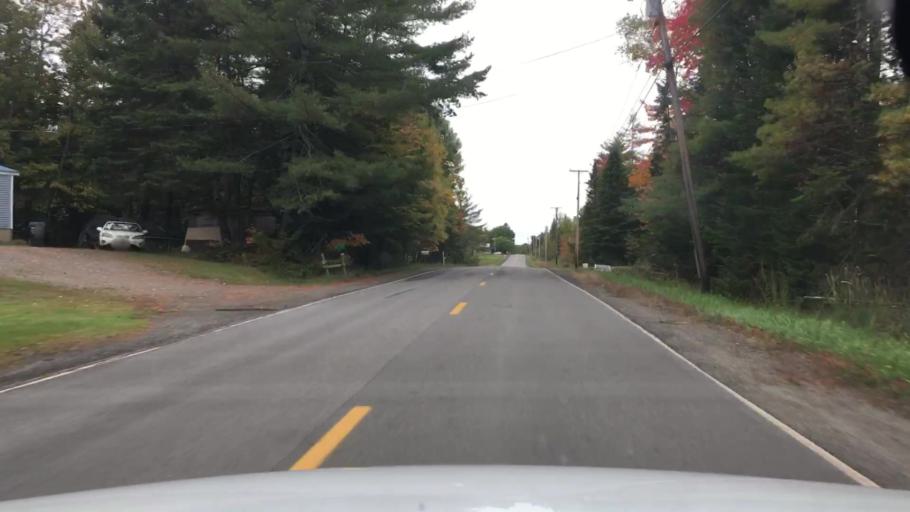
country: US
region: Maine
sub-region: Penobscot County
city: Hudson
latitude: 44.9883
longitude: -68.7618
